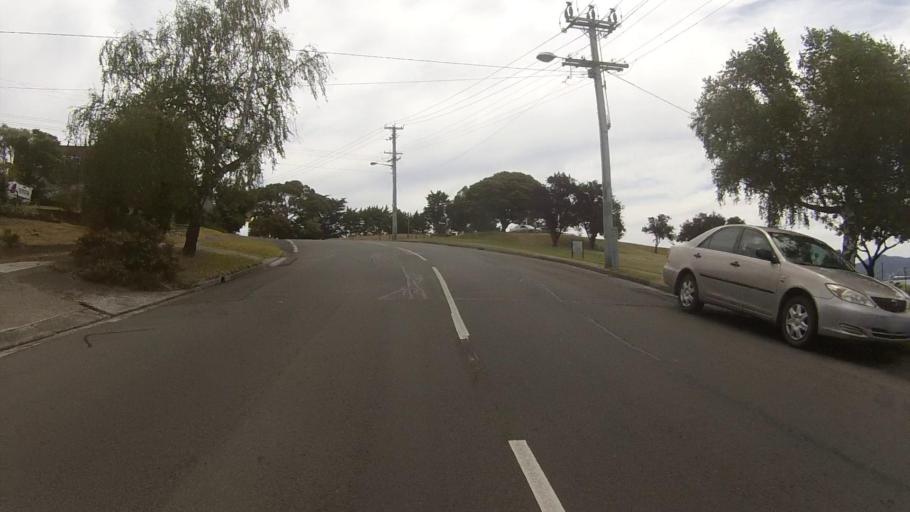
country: AU
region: Tasmania
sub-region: Kingborough
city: Taroona
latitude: -42.9164
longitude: 147.3577
